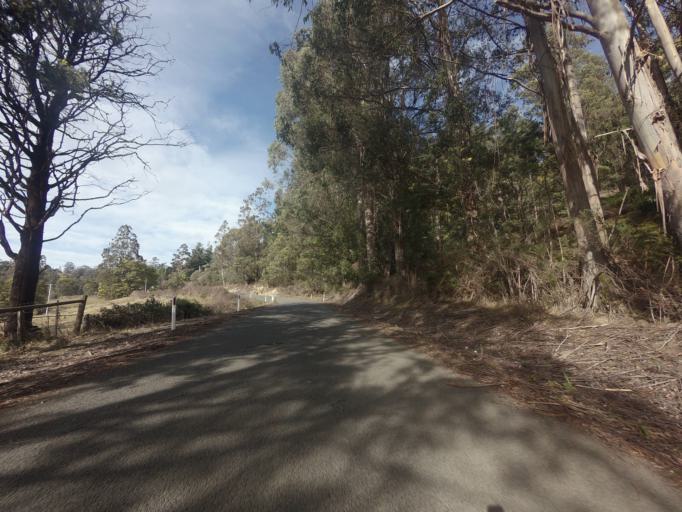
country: AU
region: Tasmania
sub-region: Kingborough
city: Margate
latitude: -43.0148
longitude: 147.1609
